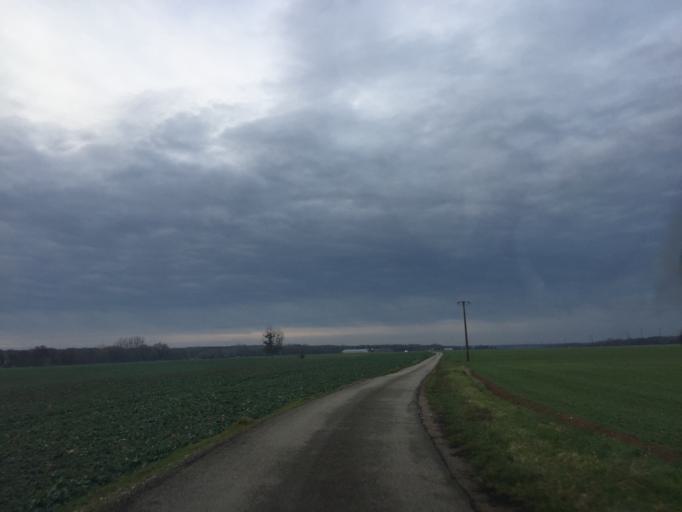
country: FR
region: Franche-Comte
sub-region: Departement du Jura
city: Mont-sous-Vaudrey
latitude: 46.9426
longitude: 5.6690
